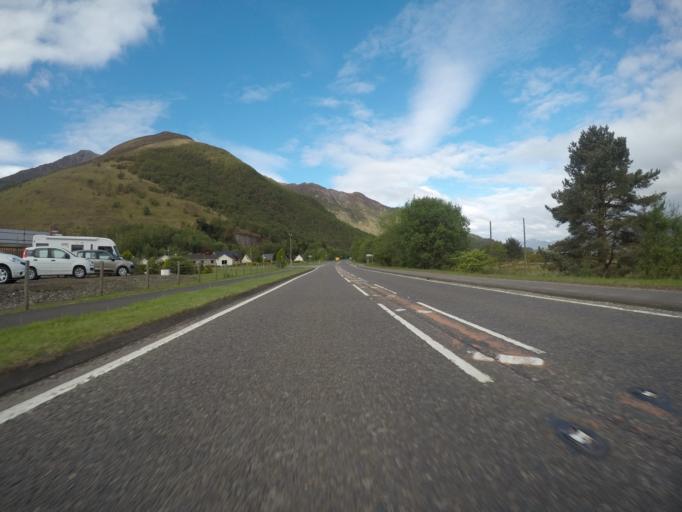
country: GB
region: Scotland
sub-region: Highland
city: Fort William
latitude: 56.6775
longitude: -5.1394
